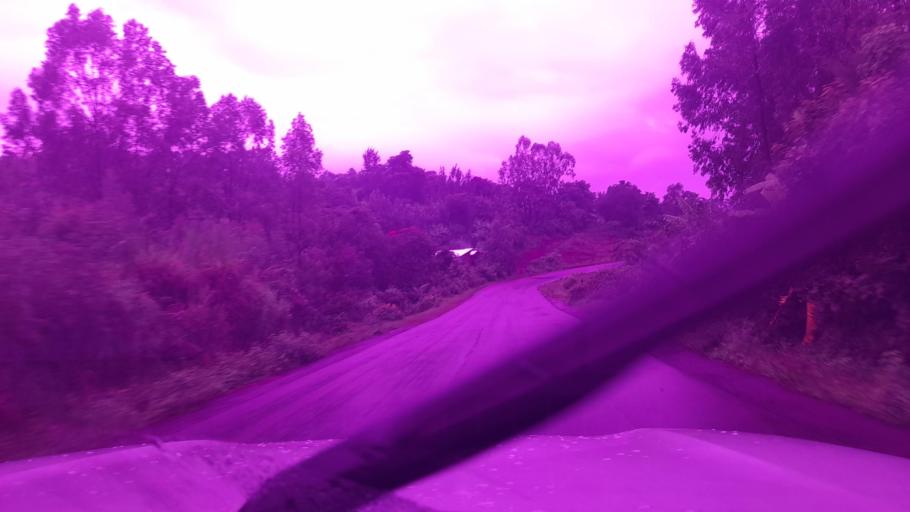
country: ET
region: Oromiya
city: Jima
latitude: 7.8041
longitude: 37.3444
